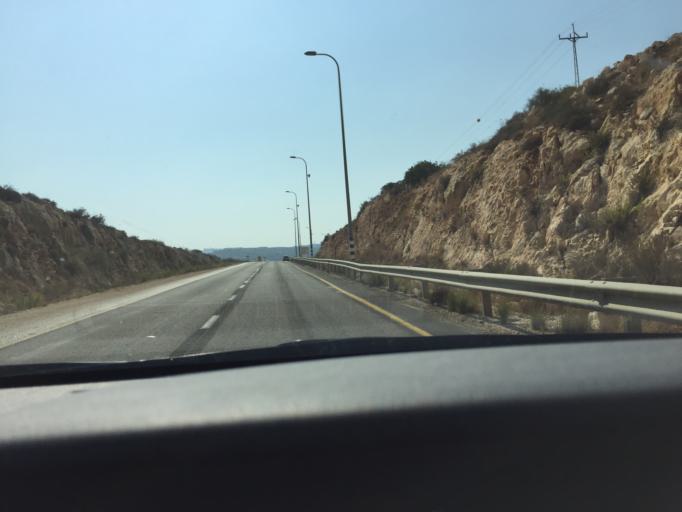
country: PS
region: West Bank
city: Bruqin
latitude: 32.0798
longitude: 35.0988
